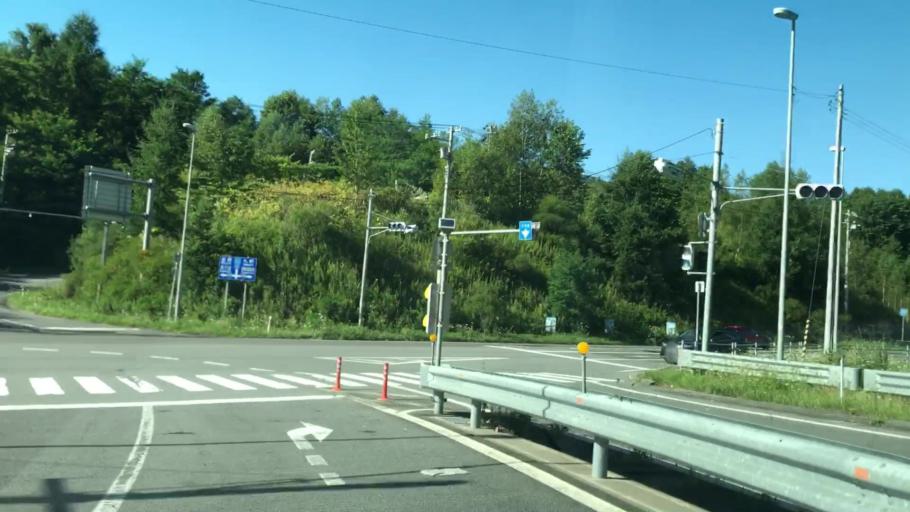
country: JP
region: Hokkaido
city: Date
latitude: 42.5587
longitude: 140.7778
